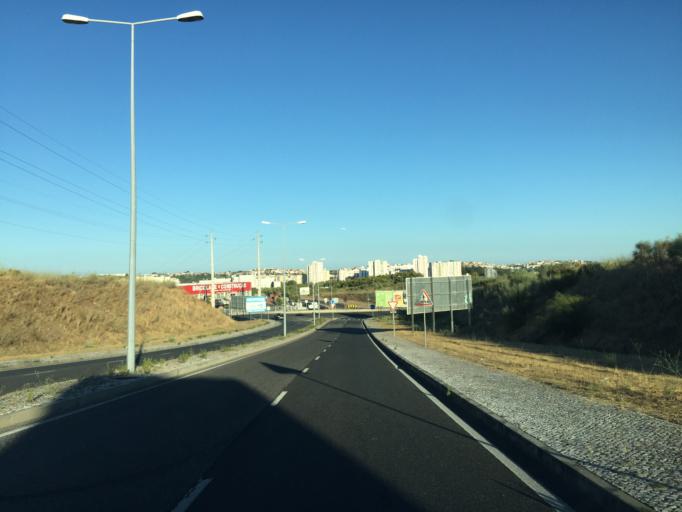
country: PT
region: Lisbon
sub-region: Loures
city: Loures
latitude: 38.8175
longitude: -9.1798
